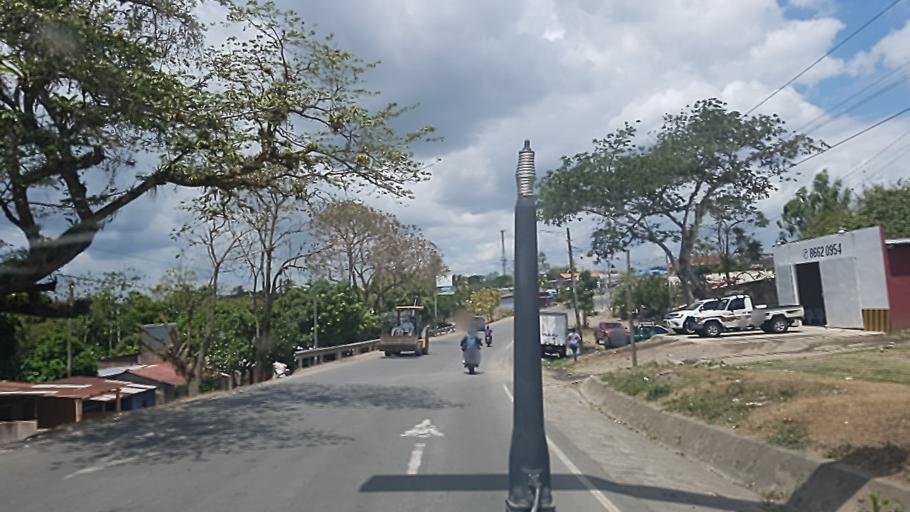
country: NI
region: Chontales
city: Santo Tomas
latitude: 12.0701
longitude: -85.0966
